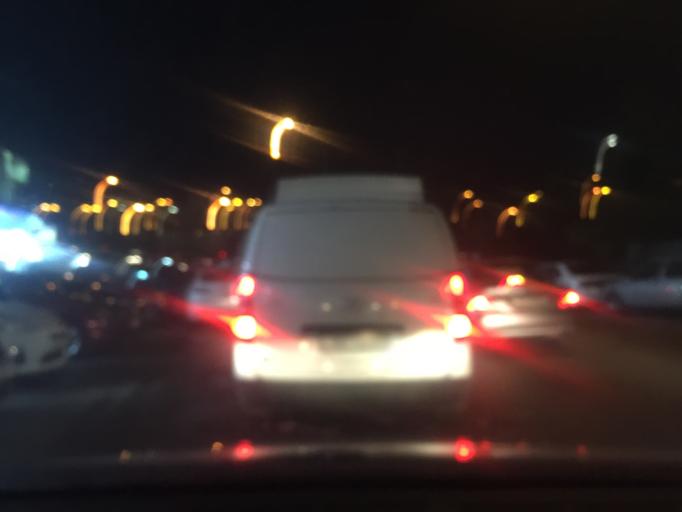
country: JO
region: Amman
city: Amman
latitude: 31.9933
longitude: 35.9177
